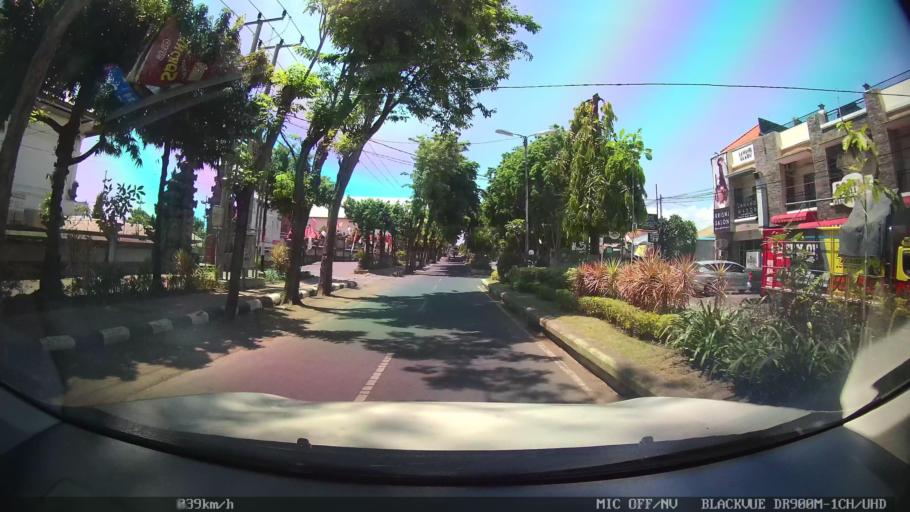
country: ID
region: Bali
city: Singaraja
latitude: -8.1157
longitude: 115.0887
